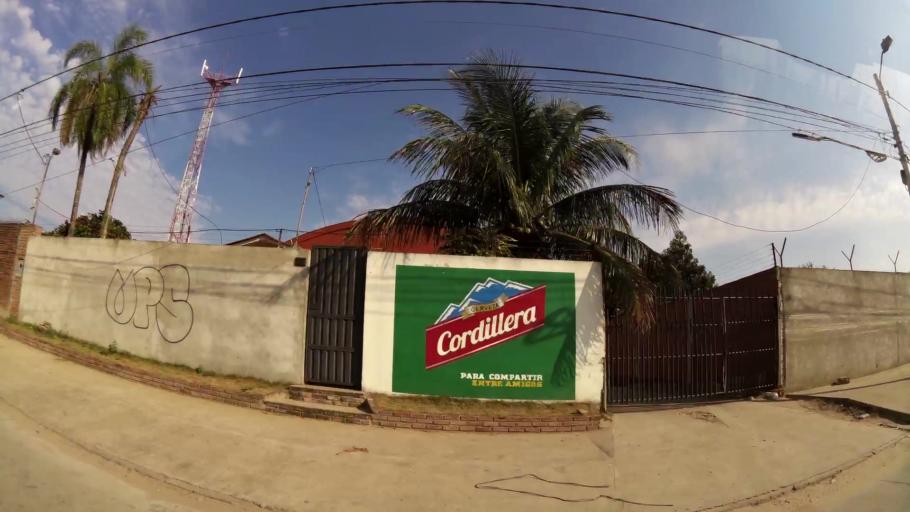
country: BO
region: Santa Cruz
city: Santa Cruz de la Sierra
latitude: -17.7416
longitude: -63.1461
